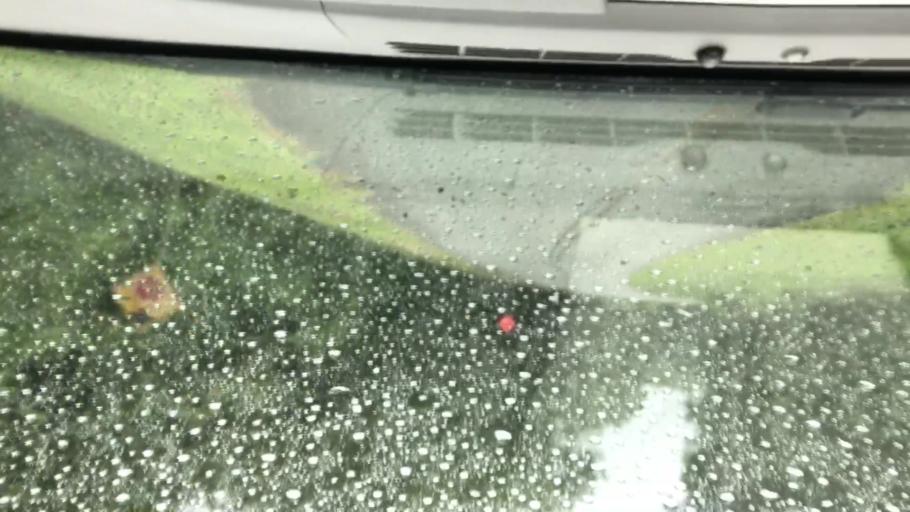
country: US
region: Georgia
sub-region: Clay County
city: Fort Gaines
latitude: 31.6637
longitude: -85.0511
